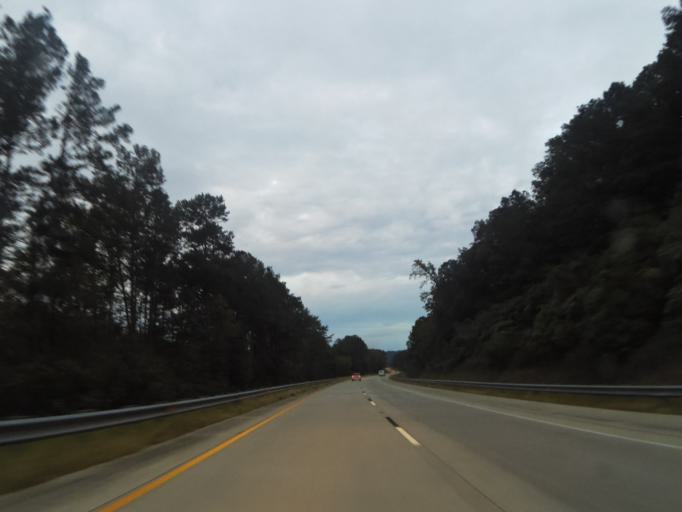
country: US
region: Alabama
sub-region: Etowah County
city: Attalla
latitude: 34.0368
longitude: -86.0714
